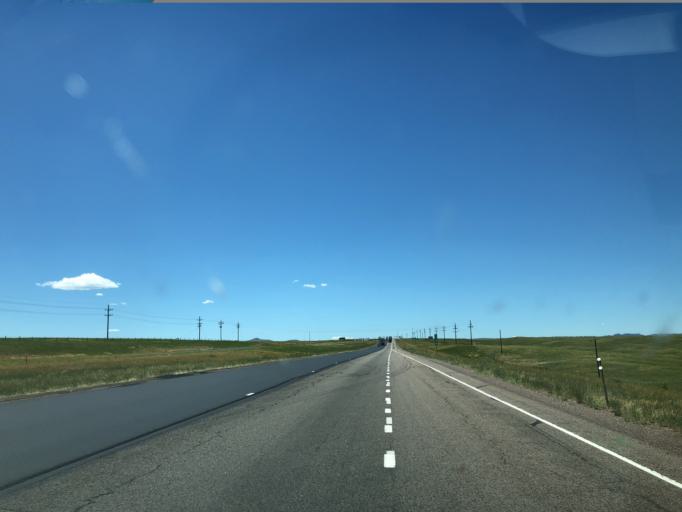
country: US
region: Wyoming
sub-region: Laramie County
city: Cheyenne
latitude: 41.1002
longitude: -105.0675
